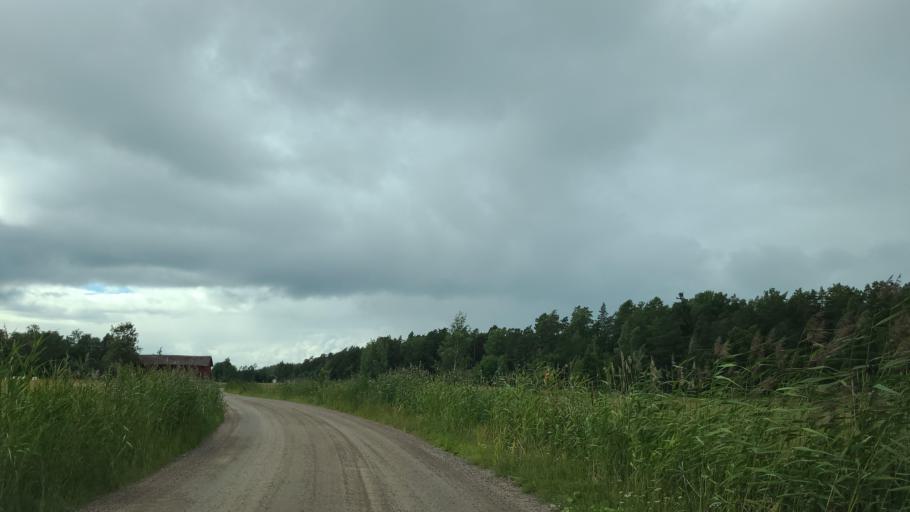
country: FI
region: Varsinais-Suomi
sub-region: Aboland-Turunmaa
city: Nagu
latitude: 60.2032
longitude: 21.8734
